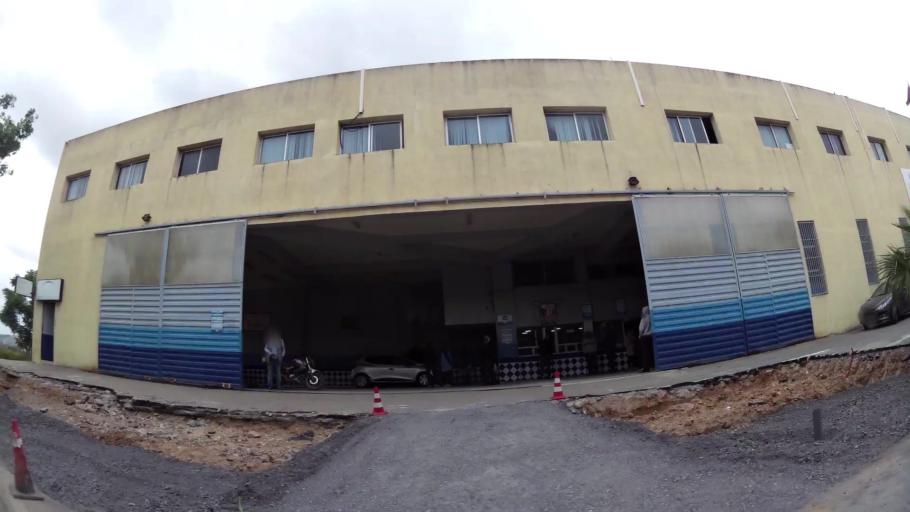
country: MA
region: Rabat-Sale-Zemmour-Zaer
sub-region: Rabat
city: Rabat
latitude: 33.9876
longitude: -6.8036
